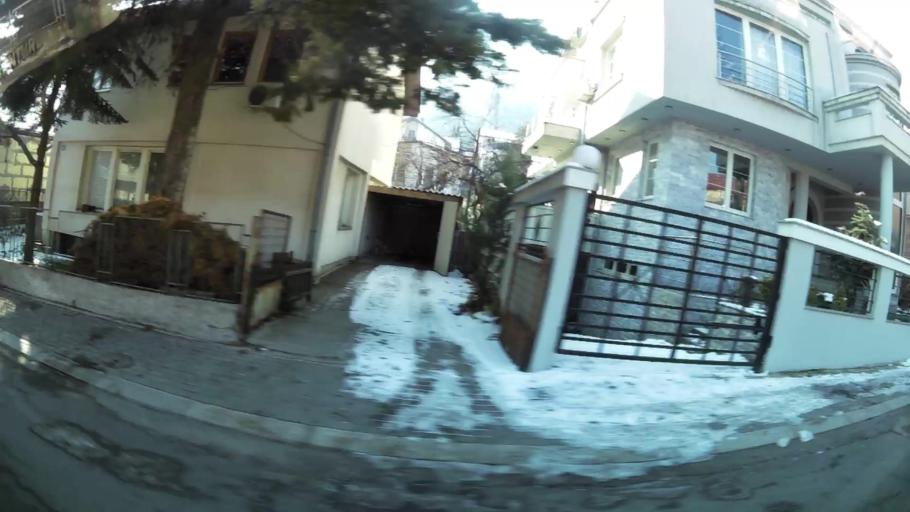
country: MK
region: Karpos
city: Skopje
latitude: 41.9774
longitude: 21.4308
